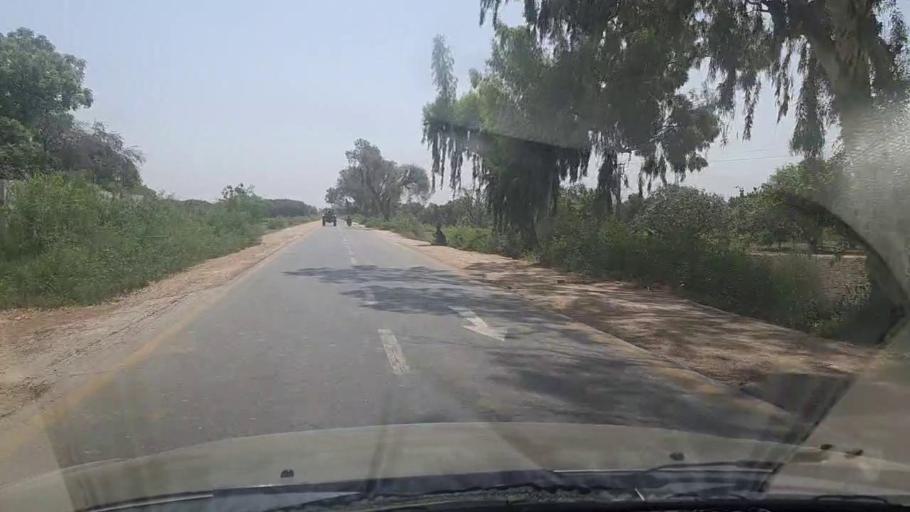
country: PK
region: Sindh
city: Tando Jam
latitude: 25.3362
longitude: 68.5315
